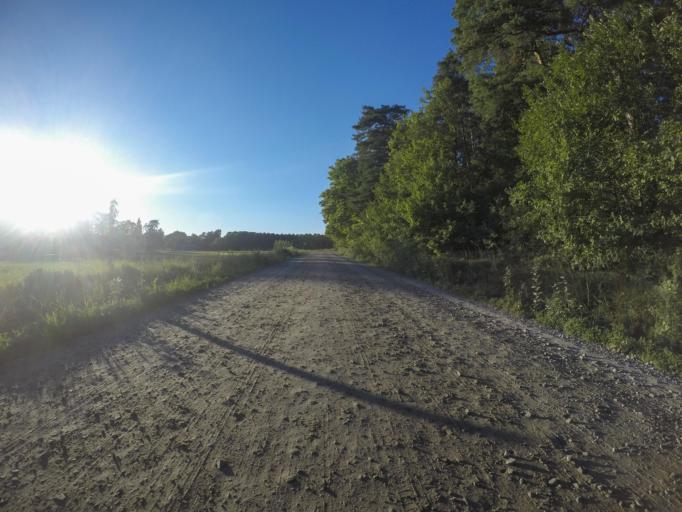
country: SE
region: Vaestmanland
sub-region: Vasteras
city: Vasteras
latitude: 59.5522
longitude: 16.6650
